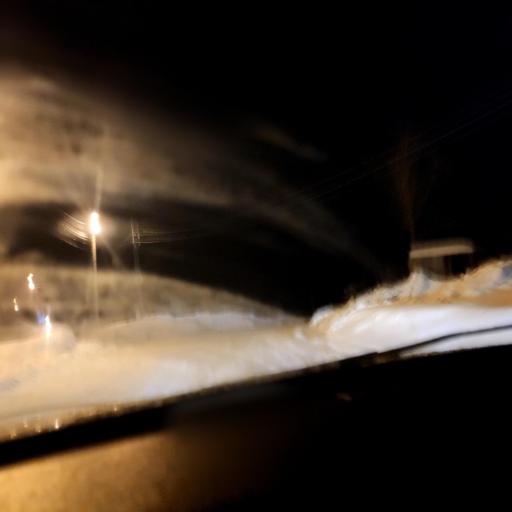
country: RU
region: Perm
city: Polazna
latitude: 58.1765
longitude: 56.3958
